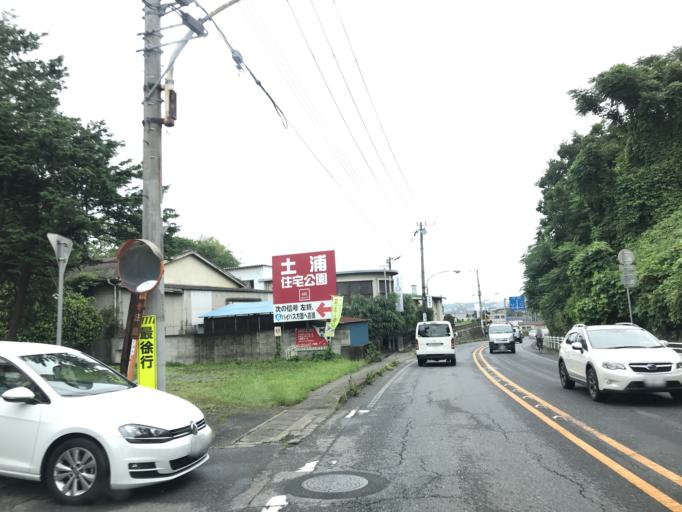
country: JP
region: Ibaraki
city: Naka
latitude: 36.0744
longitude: 140.1882
